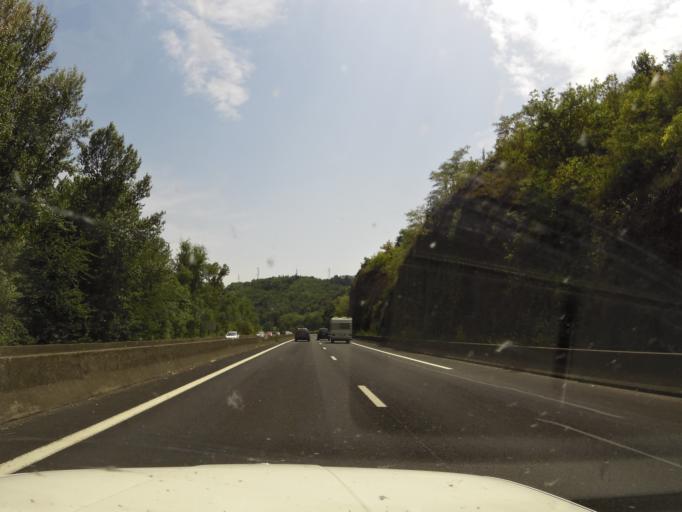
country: FR
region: Auvergne
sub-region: Departement du Puy-de-Dome
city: Vic-le-Comte
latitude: 45.6033
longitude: 3.2171
